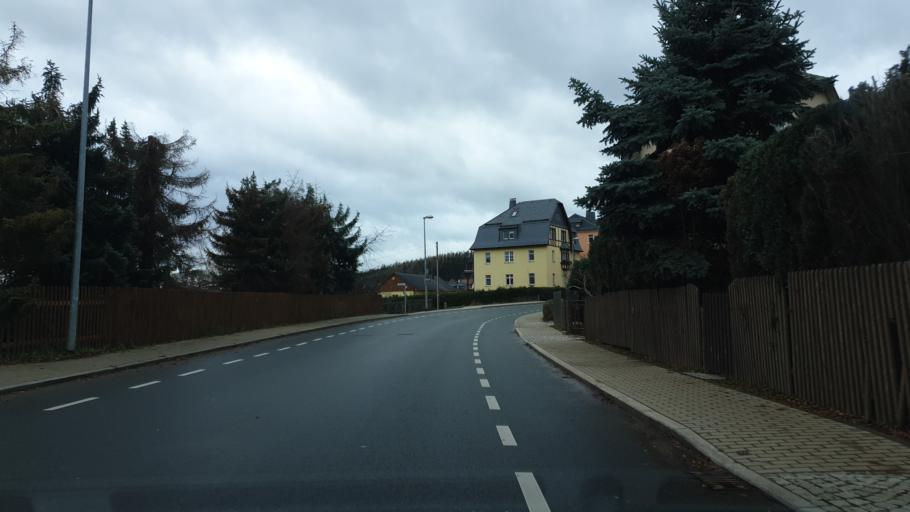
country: DE
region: Saxony
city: Hohndorf
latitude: 50.7473
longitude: 12.6663
